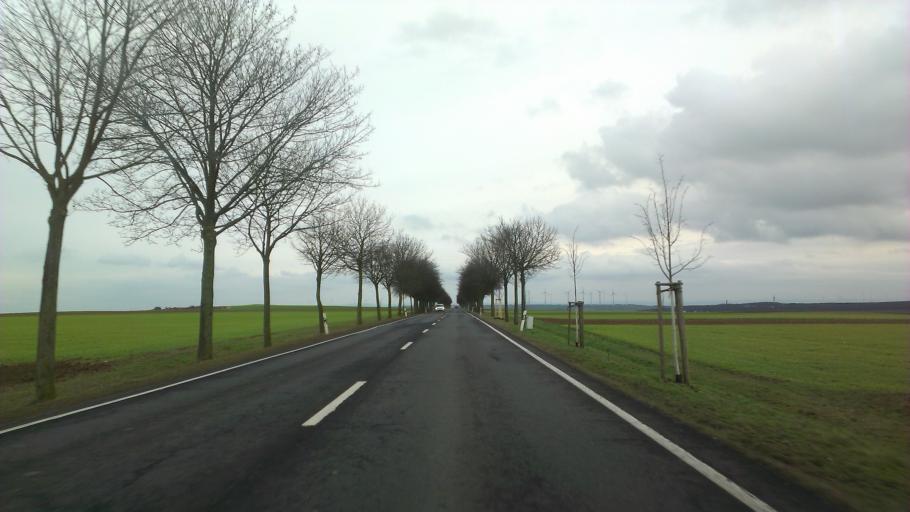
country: DE
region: Rheinland-Pfalz
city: Lonsheim
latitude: 49.7511
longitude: 8.0639
